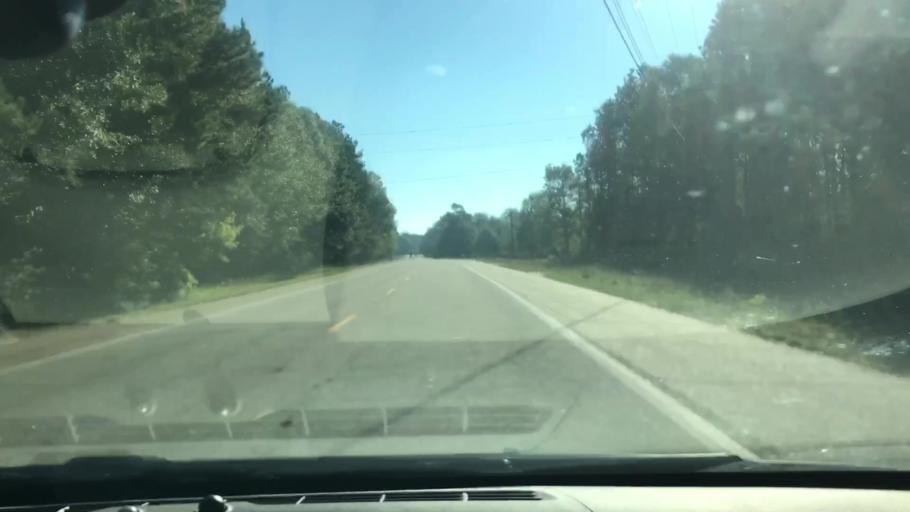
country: US
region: Mississippi
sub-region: Pearl River County
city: Nicholson
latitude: 30.5164
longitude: -89.8323
